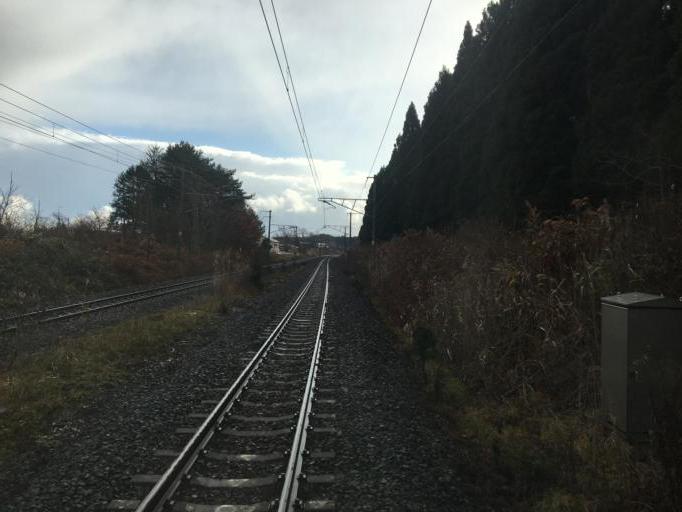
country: JP
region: Aomori
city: Aomori Shi
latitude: 40.9185
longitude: 141.0304
